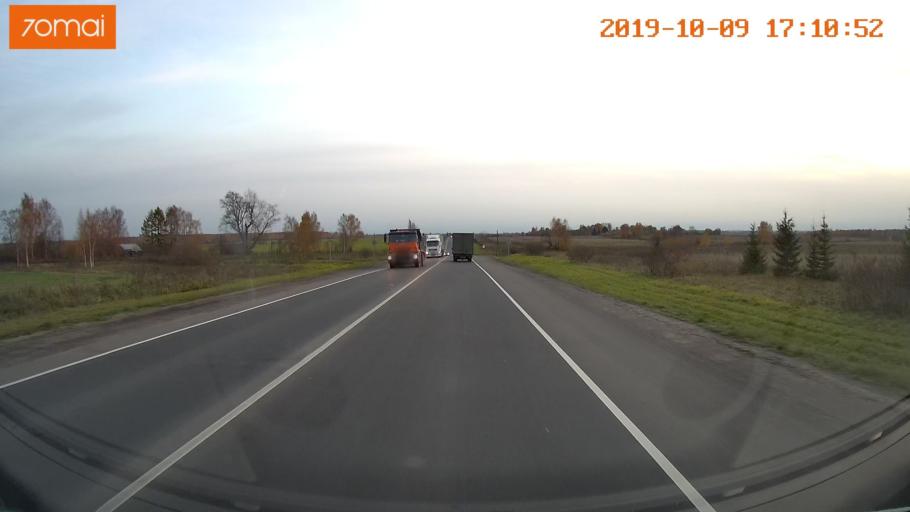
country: RU
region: Ivanovo
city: Privolzhsk
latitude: 57.3499
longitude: 41.2540
